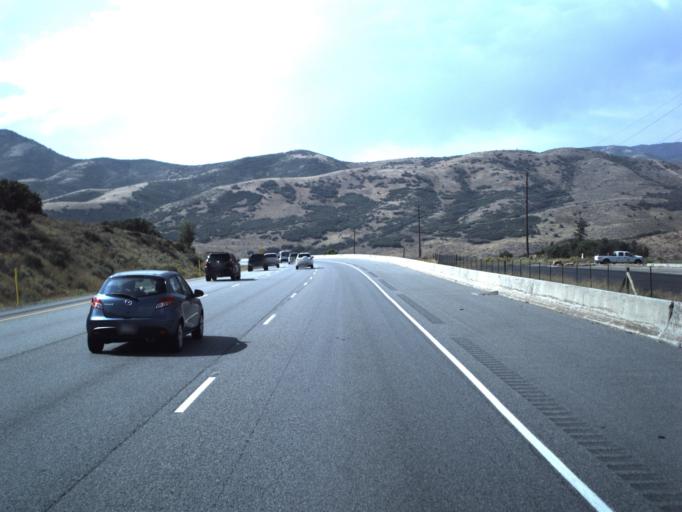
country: US
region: Utah
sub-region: Summit County
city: Summit Park
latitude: 40.7495
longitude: -111.6998
